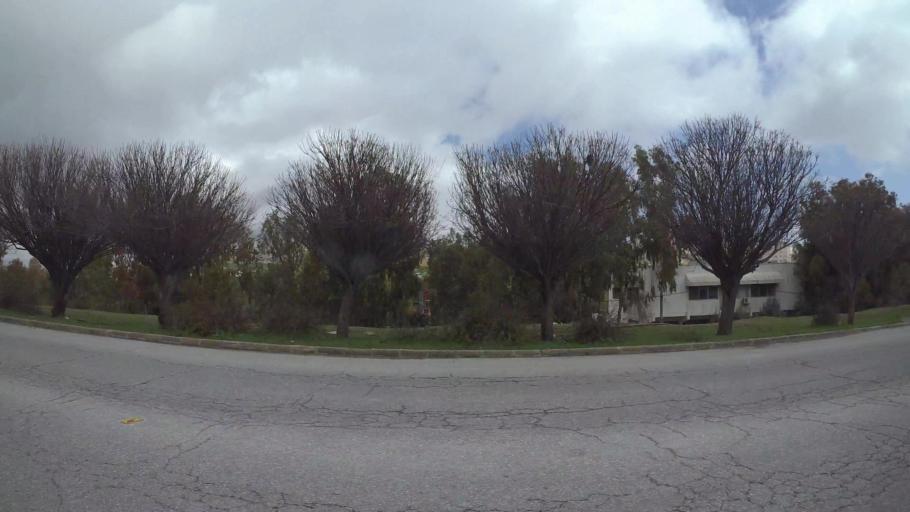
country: JO
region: Amman
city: Al Jubayhah
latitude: 32.0660
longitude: 35.8855
